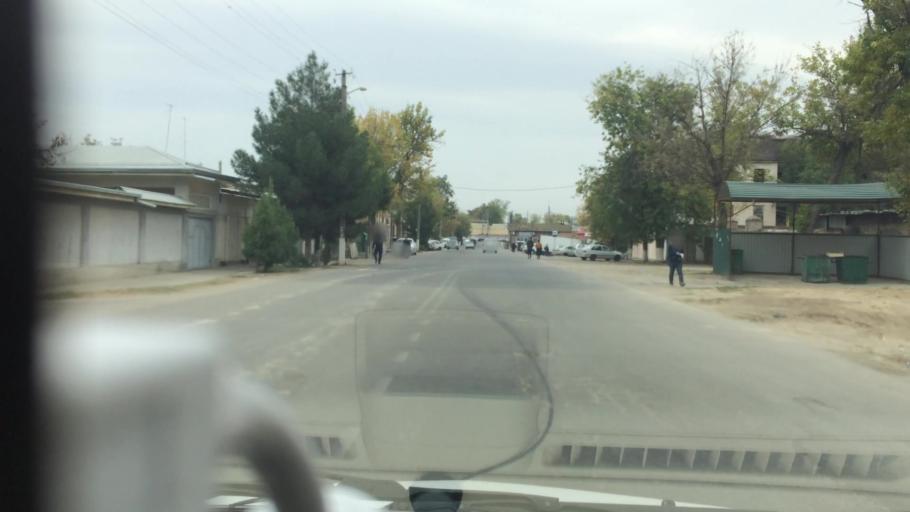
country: UZ
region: Toshkent Shahri
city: Tashkent
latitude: 41.2796
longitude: 69.2700
